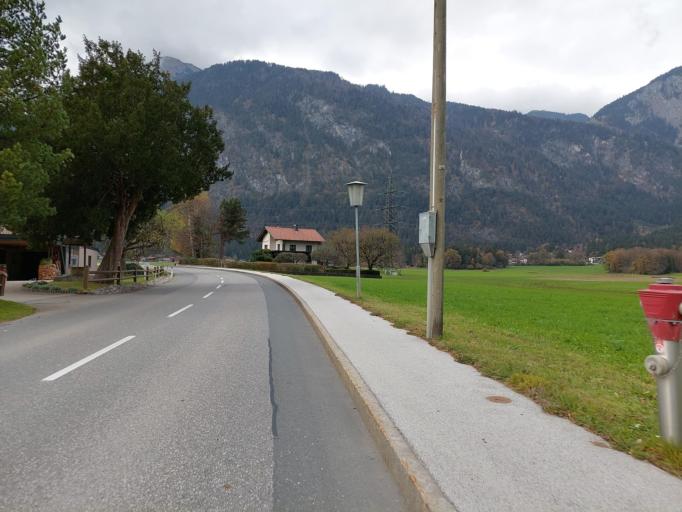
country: AT
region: Tyrol
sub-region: Politischer Bezirk Kufstein
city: Munster
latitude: 47.4283
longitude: 11.8515
